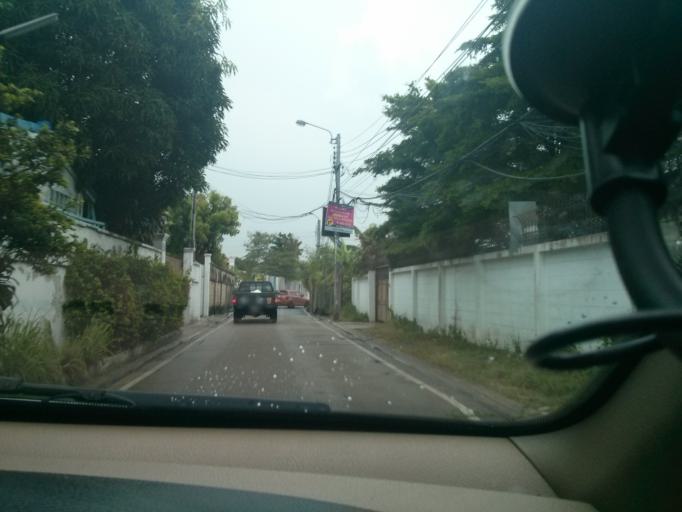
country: TH
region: Nonthaburi
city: Mueang Nonthaburi
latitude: 13.8413
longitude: 100.5163
